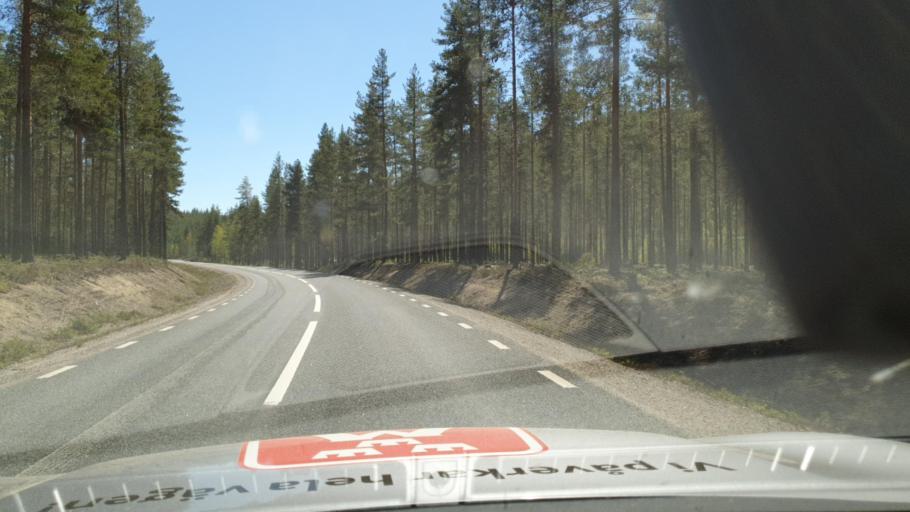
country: SE
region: Vaesternorrland
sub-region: OErnskoeldsviks Kommun
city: Bredbyn
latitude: 63.8105
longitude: 18.4824
